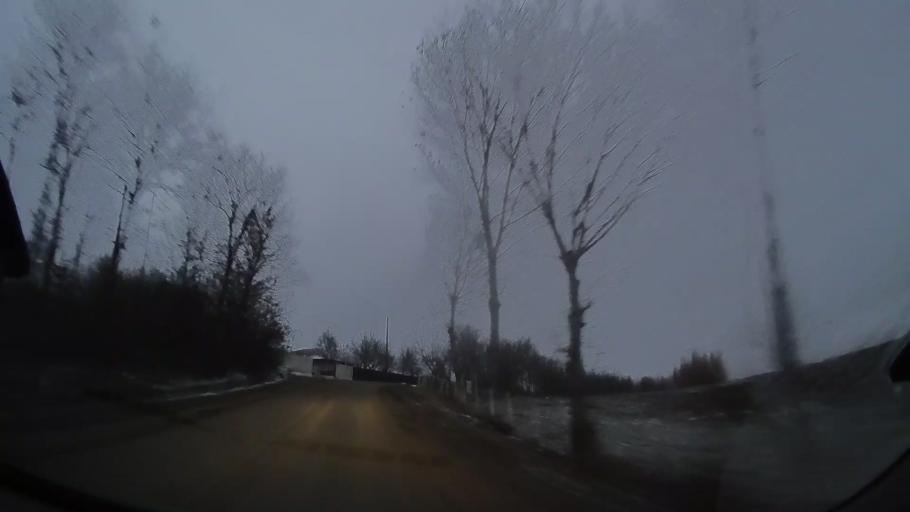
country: RO
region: Vaslui
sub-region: Comuna Vutcani
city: Vutcani
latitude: 46.4175
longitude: 27.9975
